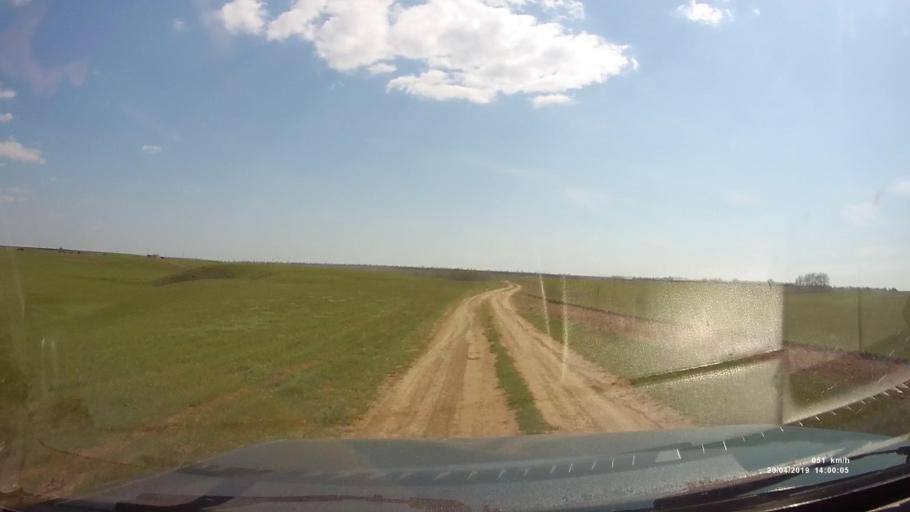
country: RU
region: Rostov
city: Remontnoye
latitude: 46.5619
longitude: 42.9469
